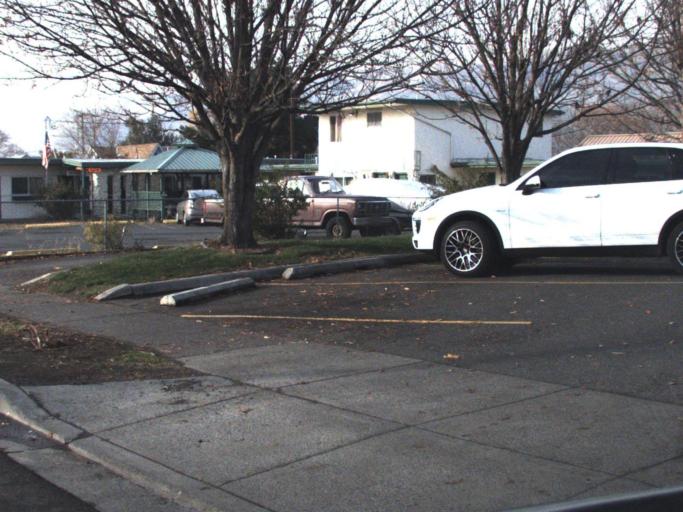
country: US
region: Washington
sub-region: Asotin County
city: Clarkston
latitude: 46.4199
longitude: -117.0489
